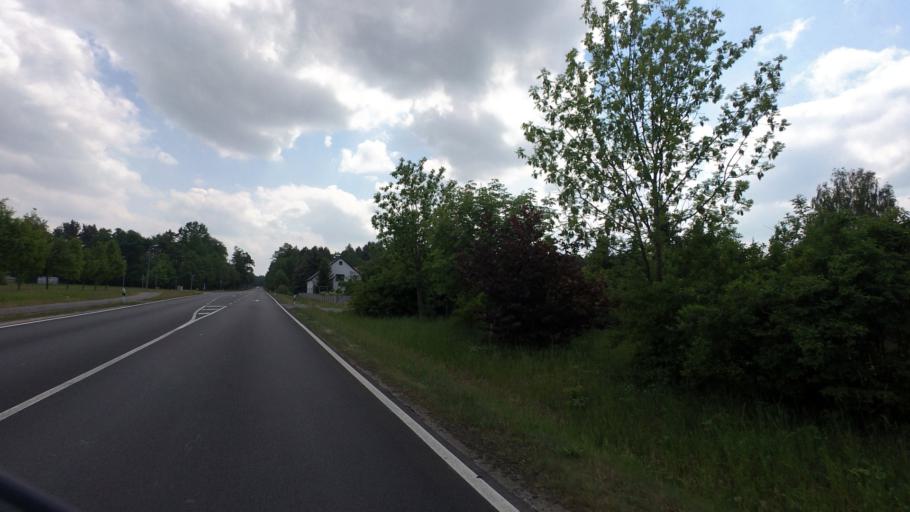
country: DE
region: Saxony
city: Rietschen
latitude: 51.3836
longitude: 14.7874
